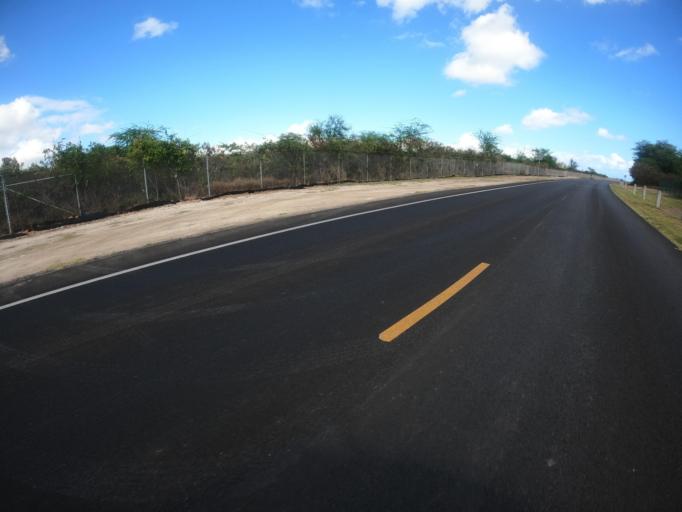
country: US
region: Hawaii
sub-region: Honolulu County
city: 'Ewa Villages
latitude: 21.3009
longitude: -158.0666
